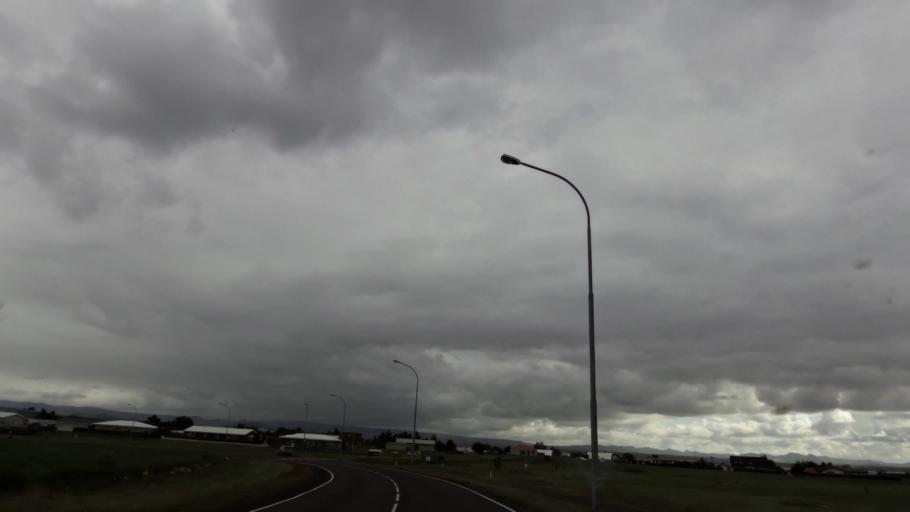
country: IS
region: Capital Region
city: Alftanes
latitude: 64.1008
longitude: -22.0266
